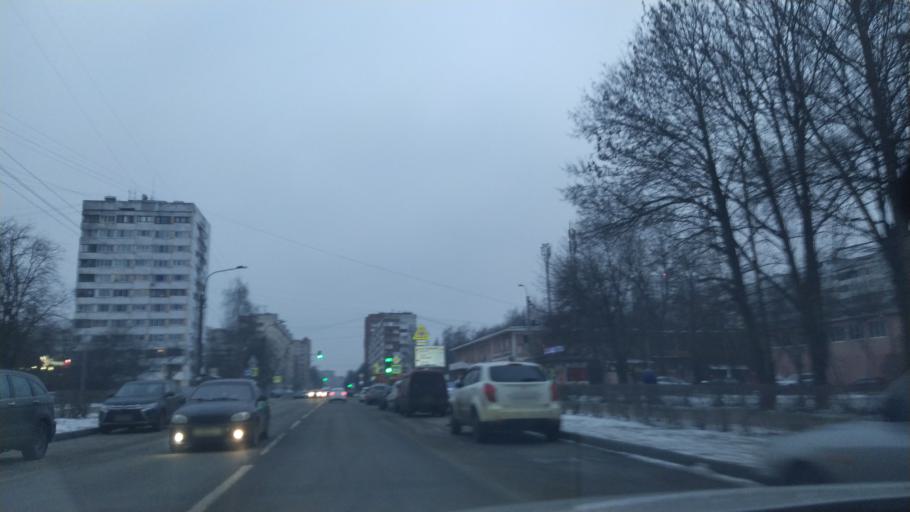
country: RU
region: St.-Petersburg
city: Grazhdanka
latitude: 60.0426
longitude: 30.4112
